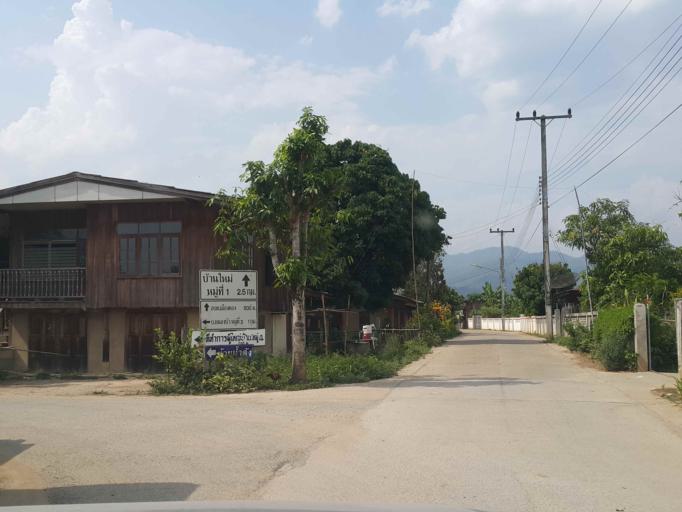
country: TH
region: Chiang Mai
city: Wiang Haeng
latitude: 19.3848
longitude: 98.7164
